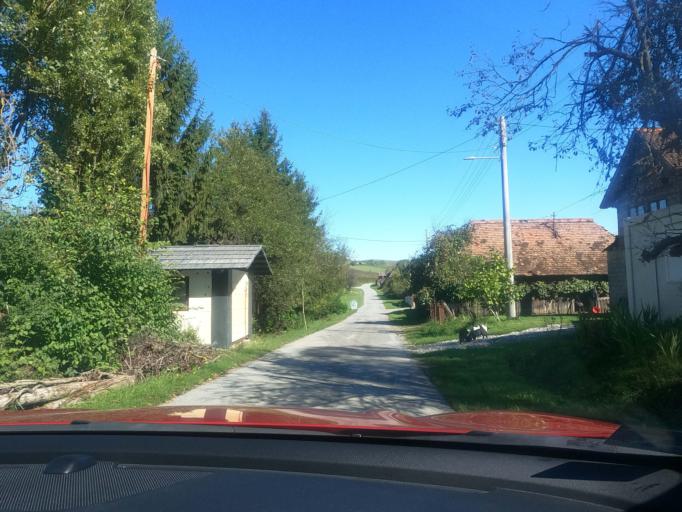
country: HR
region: Sisacko-Moslavacka
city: Petrinja
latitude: 45.3584
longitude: 16.2176
